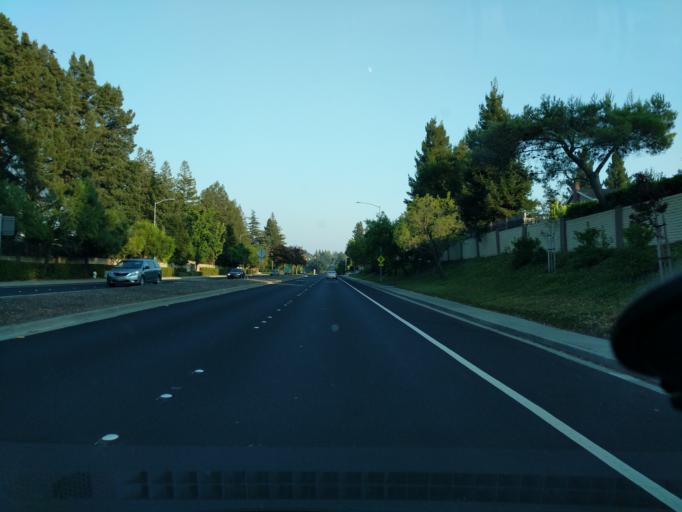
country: US
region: California
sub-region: Contra Costa County
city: San Ramon
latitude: 37.7630
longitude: -121.9821
